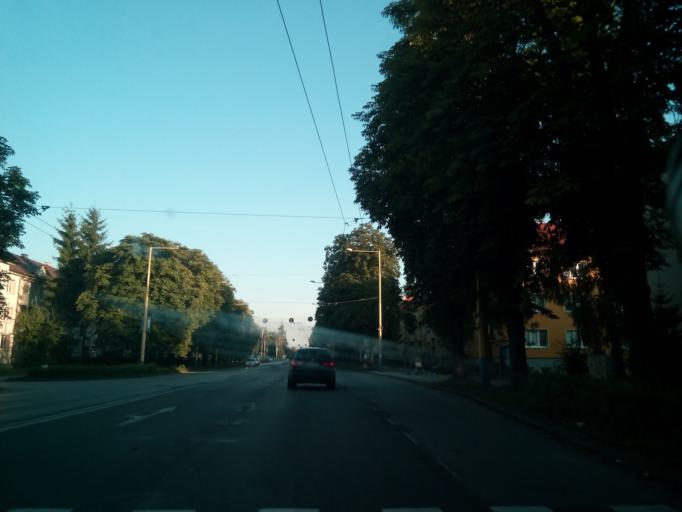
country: SK
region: Presovsky
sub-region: Okres Presov
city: Presov
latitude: 48.9976
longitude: 21.2281
